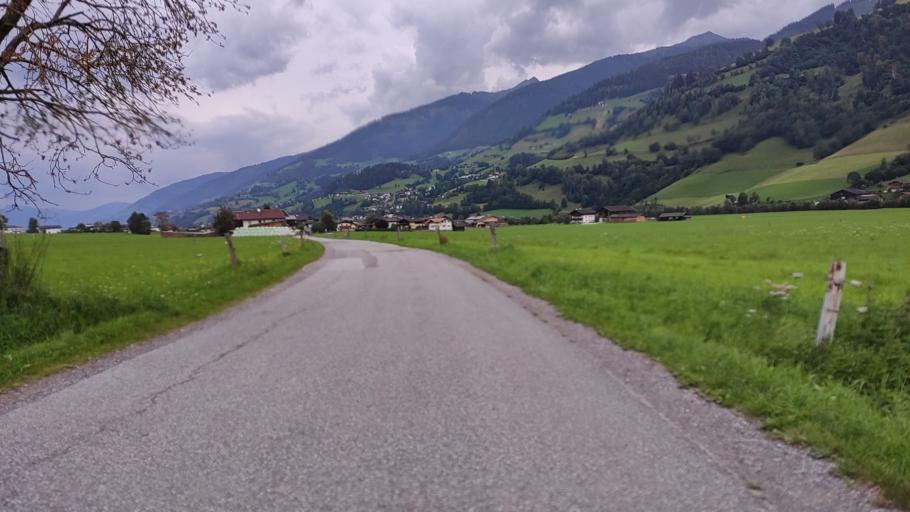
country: AT
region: Salzburg
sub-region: Politischer Bezirk Zell am See
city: Niedernsill
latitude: 47.2797
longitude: 12.6633
